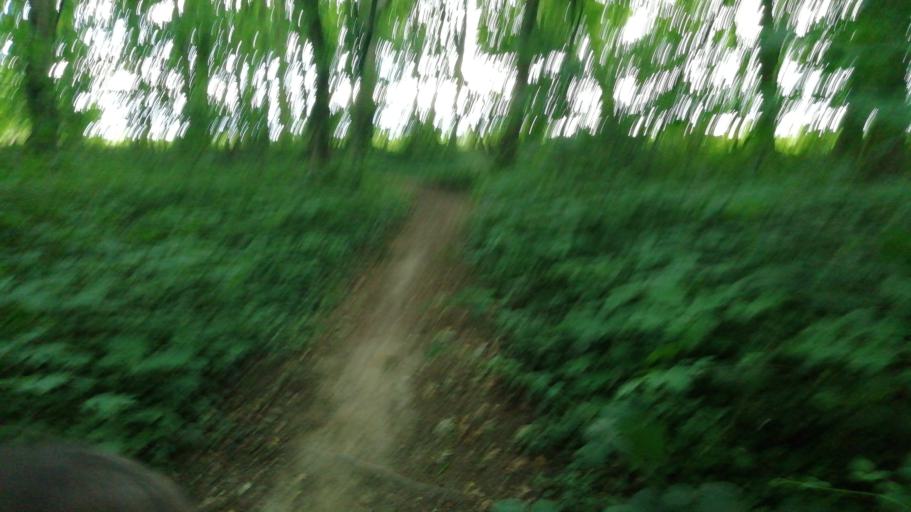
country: BE
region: Wallonia
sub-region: Province du Hainaut
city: Merbes-le-Chateau
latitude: 50.2829
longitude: 4.1819
